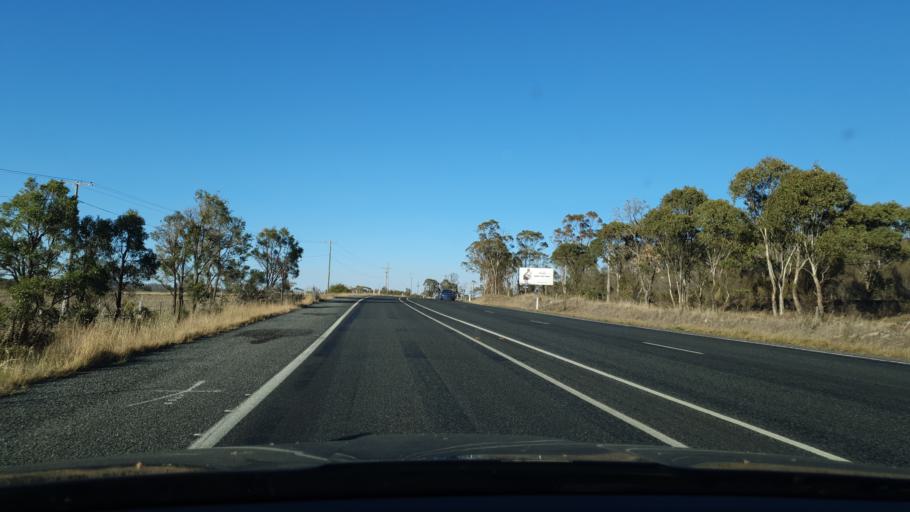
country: AU
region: Queensland
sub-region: Southern Downs
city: Stanthorpe
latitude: -28.6877
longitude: 151.9115
